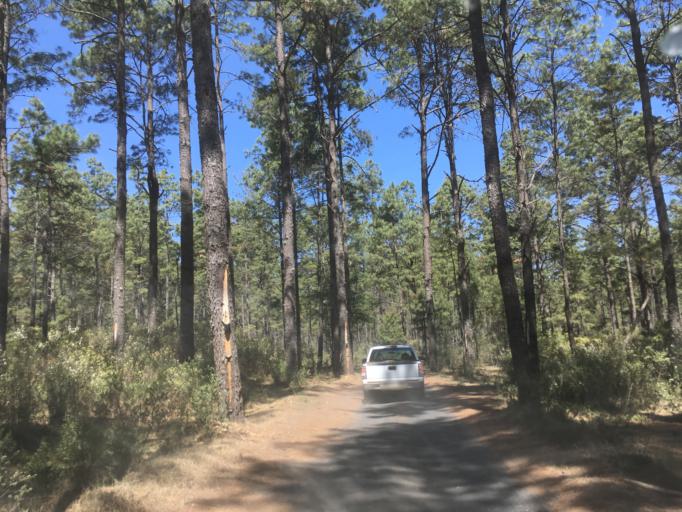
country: MX
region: Michoacan
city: Angahuan
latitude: 19.4635
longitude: -102.2262
